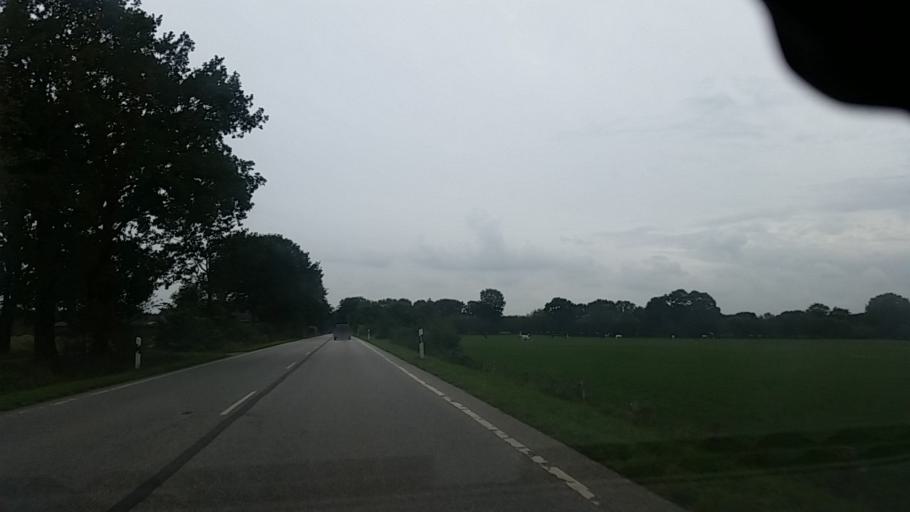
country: DE
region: Schleswig-Holstein
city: Kayhude
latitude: 53.7821
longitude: 10.1293
